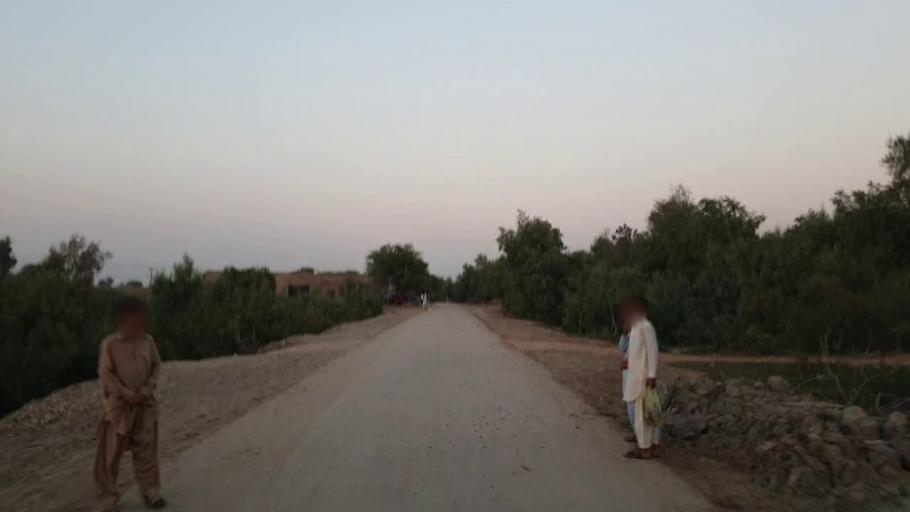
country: PK
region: Sindh
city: Bhan
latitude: 26.4676
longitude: 67.7629
